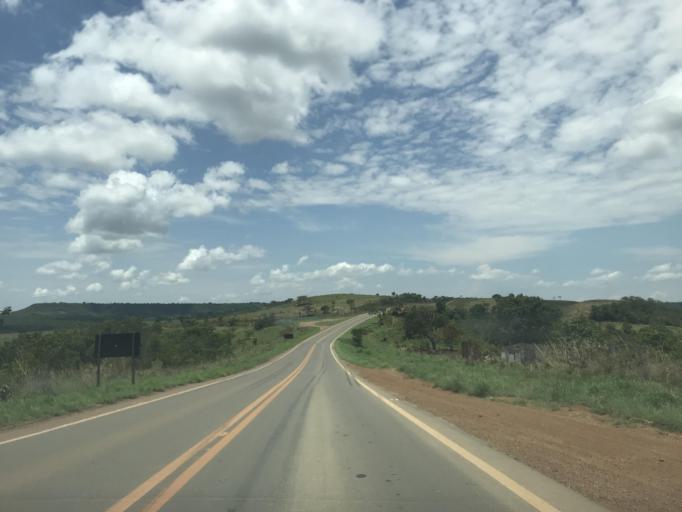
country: BR
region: Goias
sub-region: Luziania
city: Luziania
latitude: -16.4044
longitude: -48.1814
